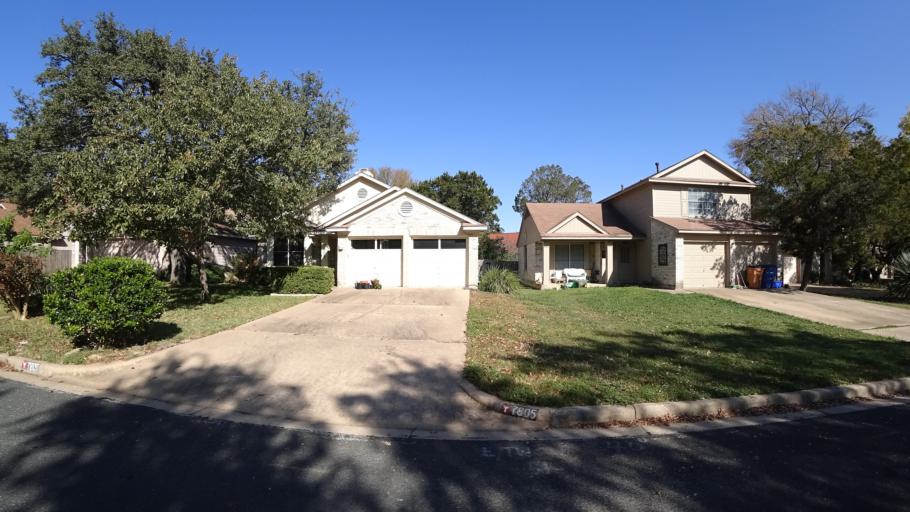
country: US
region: Texas
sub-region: Travis County
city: Shady Hollow
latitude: 30.2181
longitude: -97.8642
